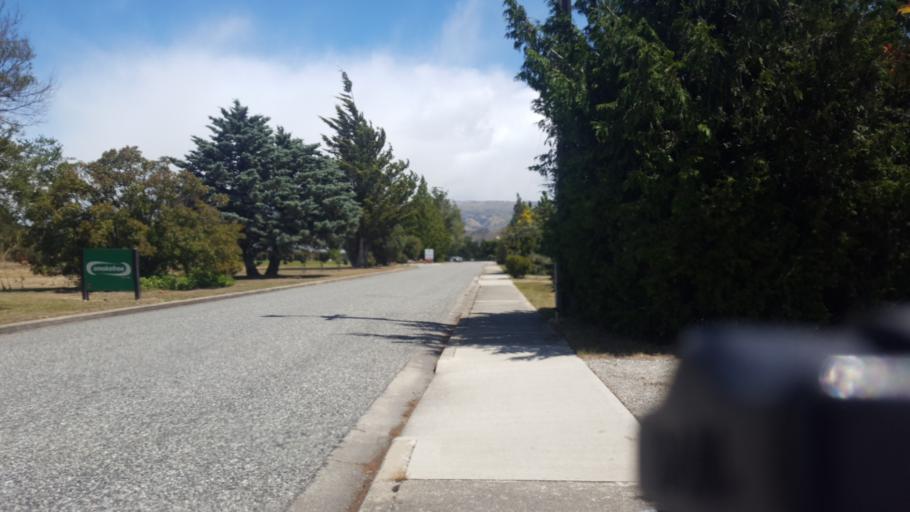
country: NZ
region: Otago
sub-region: Queenstown-Lakes District
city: Wanaka
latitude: -45.1992
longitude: 169.3317
